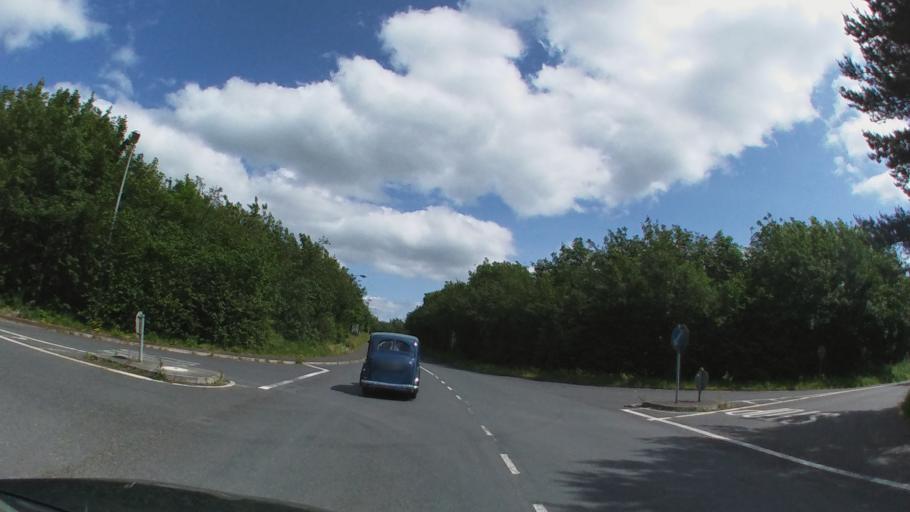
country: IE
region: Leinster
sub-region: Kildare
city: Moone
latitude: 53.0079
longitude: -6.8070
